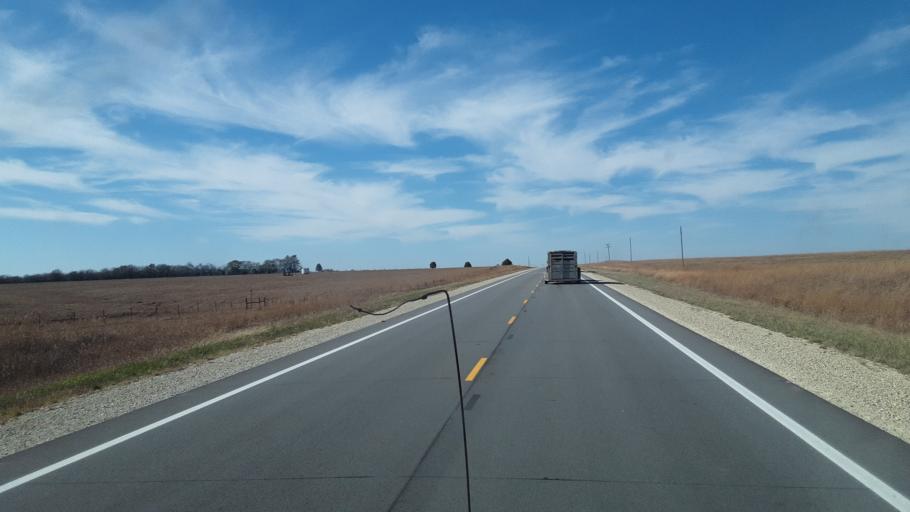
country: US
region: Kansas
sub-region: Marion County
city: Marion
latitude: 38.3629
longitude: -96.8786
